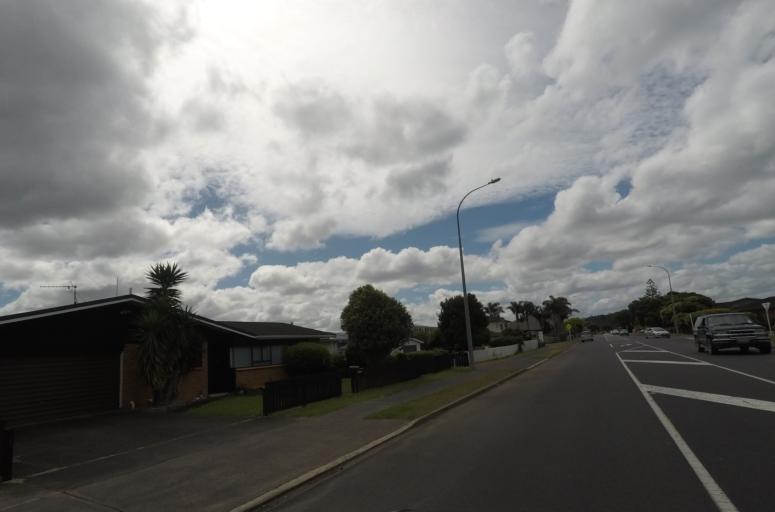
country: NZ
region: Auckland
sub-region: Auckland
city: Rothesay Bay
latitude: -36.5887
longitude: 174.6929
